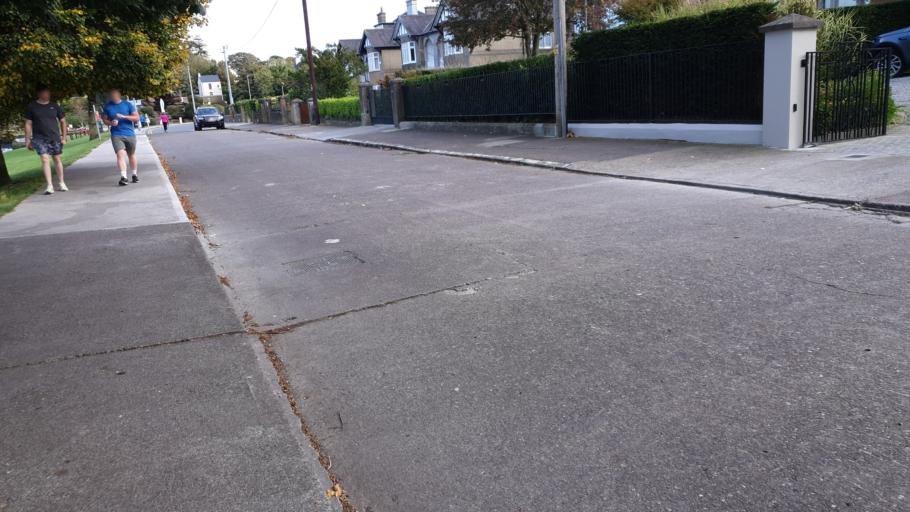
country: IE
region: Munster
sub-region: County Cork
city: Cork
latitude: 51.8983
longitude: -8.4150
